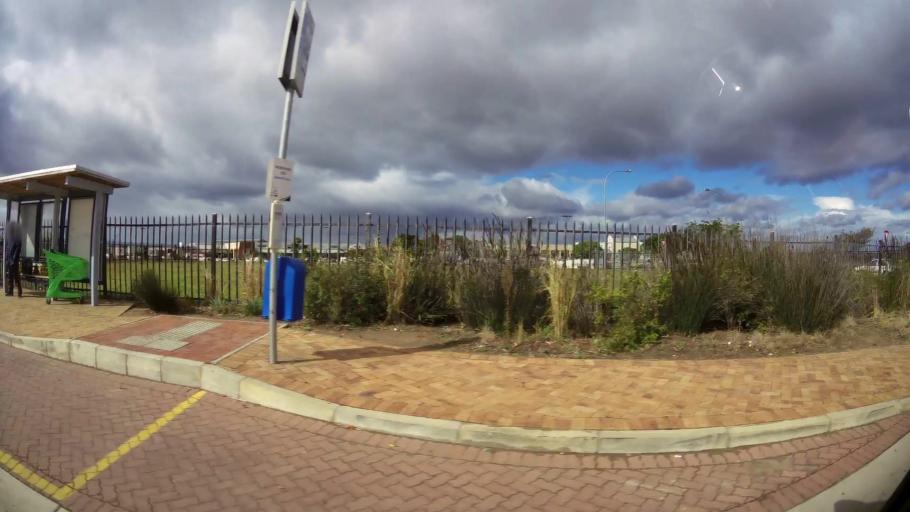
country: ZA
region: Western Cape
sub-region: Eden District Municipality
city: George
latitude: -33.9864
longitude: 22.5002
